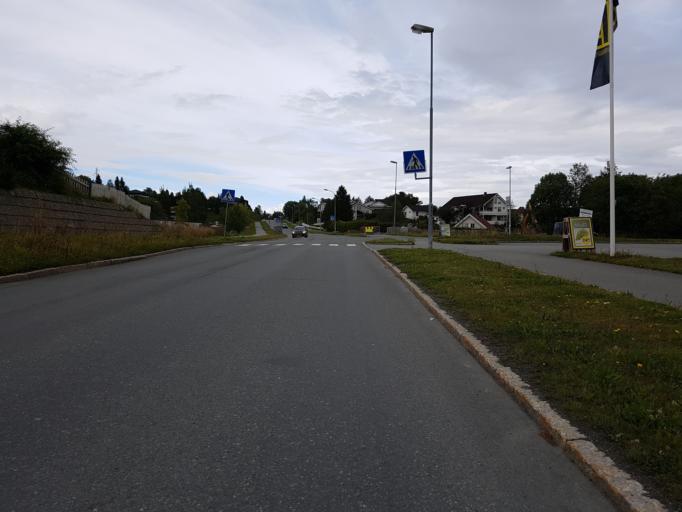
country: NO
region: Sor-Trondelag
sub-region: Trondheim
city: Trondheim
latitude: 63.3876
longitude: 10.3522
